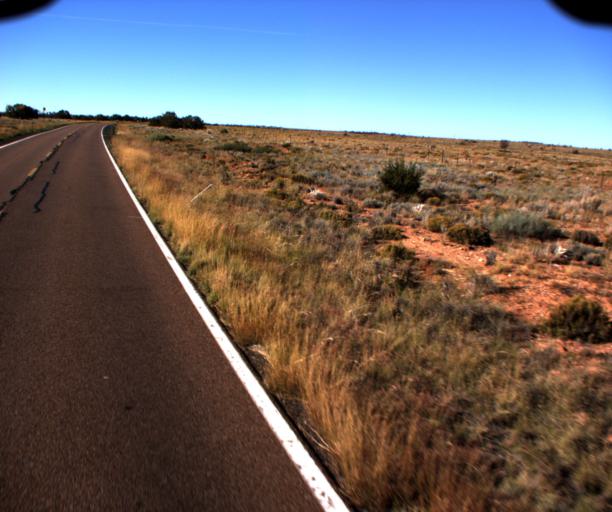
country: US
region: Arizona
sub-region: Navajo County
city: Holbrook
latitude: 34.6843
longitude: -110.3094
